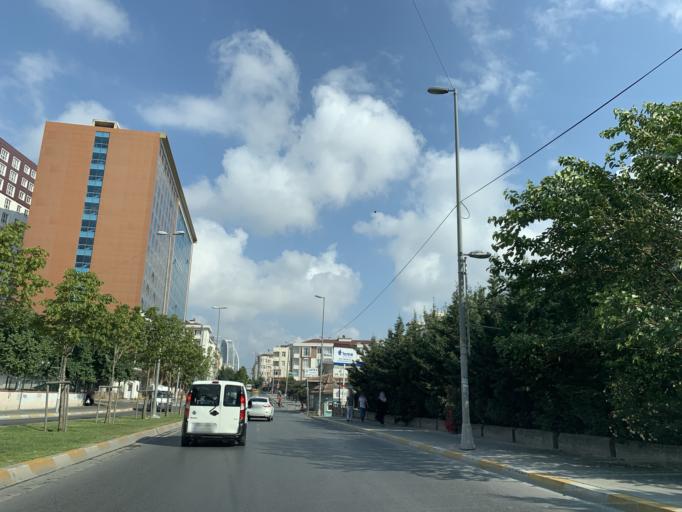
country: TR
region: Istanbul
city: Esenyurt
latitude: 41.0264
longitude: 28.6680
